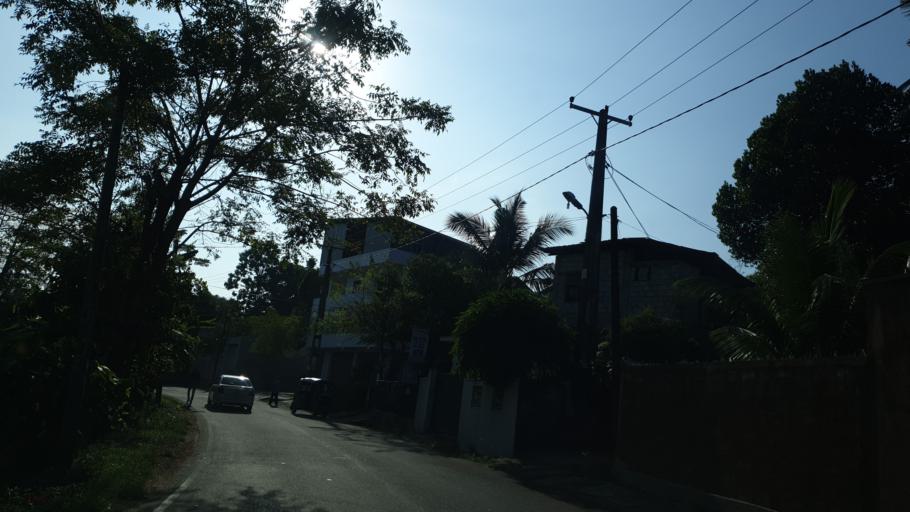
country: LK
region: Western
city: Sri Jayewardenepura Kotte
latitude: 6.8738
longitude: 79.9177
